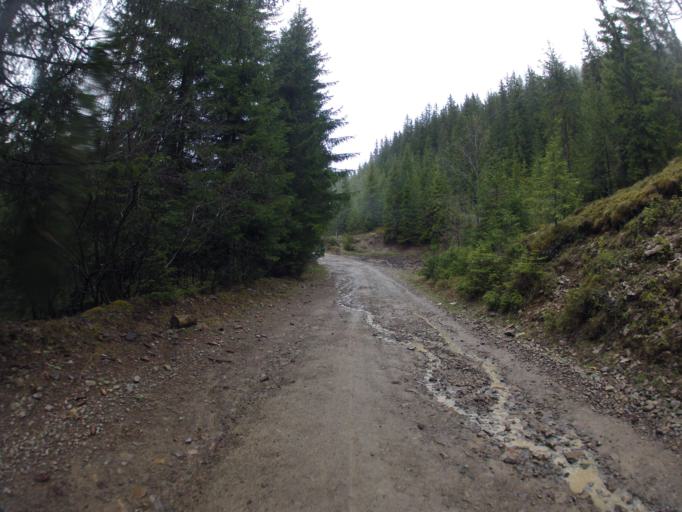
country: RO
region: Suceava
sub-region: Comuna Izvoarele Sucevei
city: Izvoarele Sucevei
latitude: 47.8195
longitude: 25.0951
